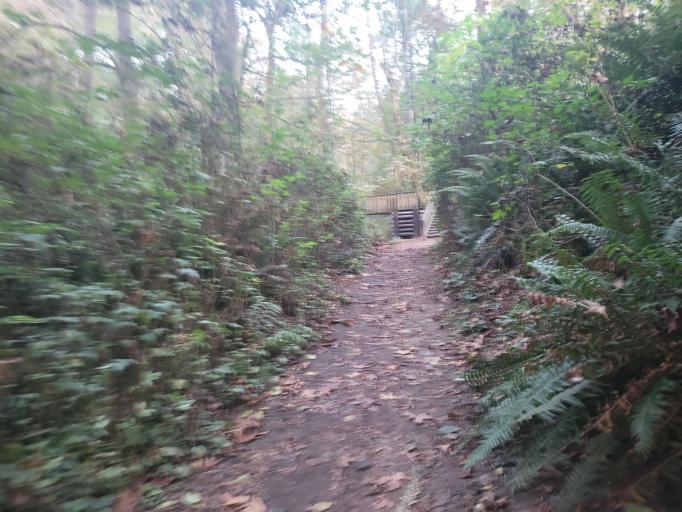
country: US
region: Washington
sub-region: Pierce County
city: Tacoma
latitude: 47.3146
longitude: -122.4123
